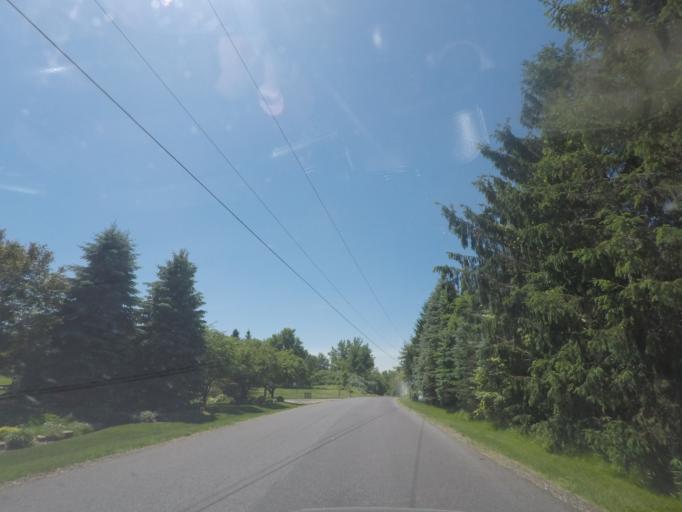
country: US
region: New York
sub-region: Saratoga County
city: Country Knolls
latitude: 42.9426
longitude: -73.7651
